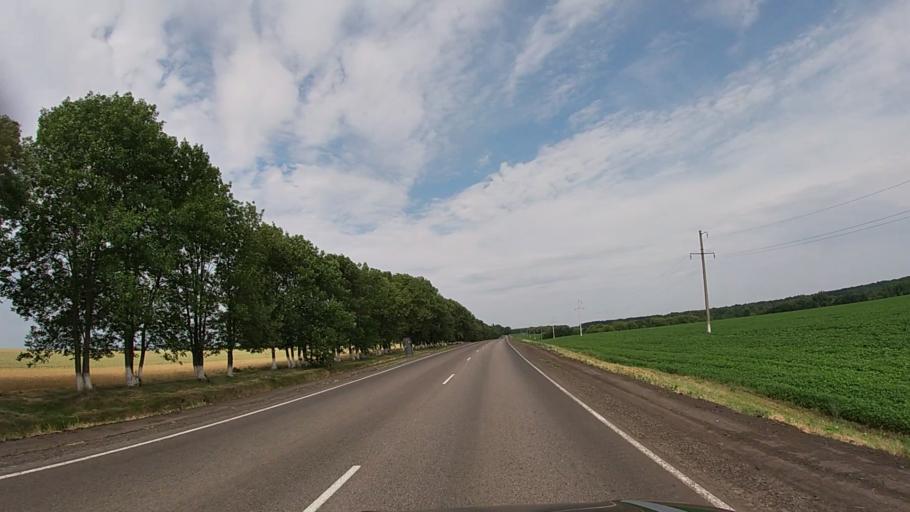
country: RU
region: Belgorod
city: Krasnaya Yaruga
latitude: 50.8091
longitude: 35.5239
